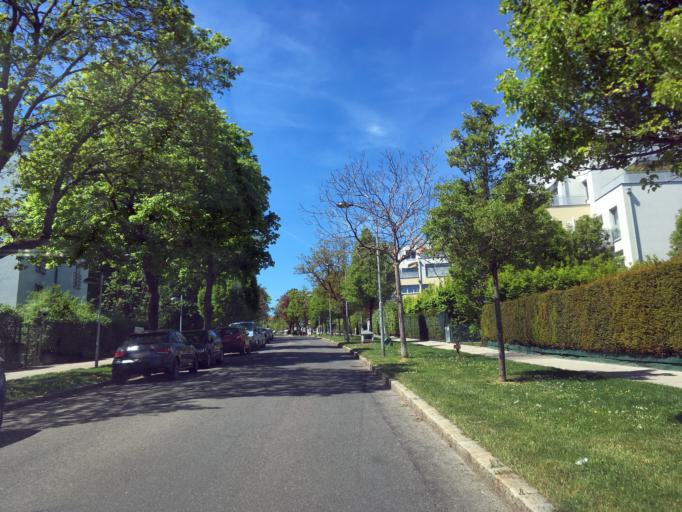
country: AT
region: Vienna
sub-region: Wien Stadt
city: Vienna
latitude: 48.2460
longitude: 16.3594
